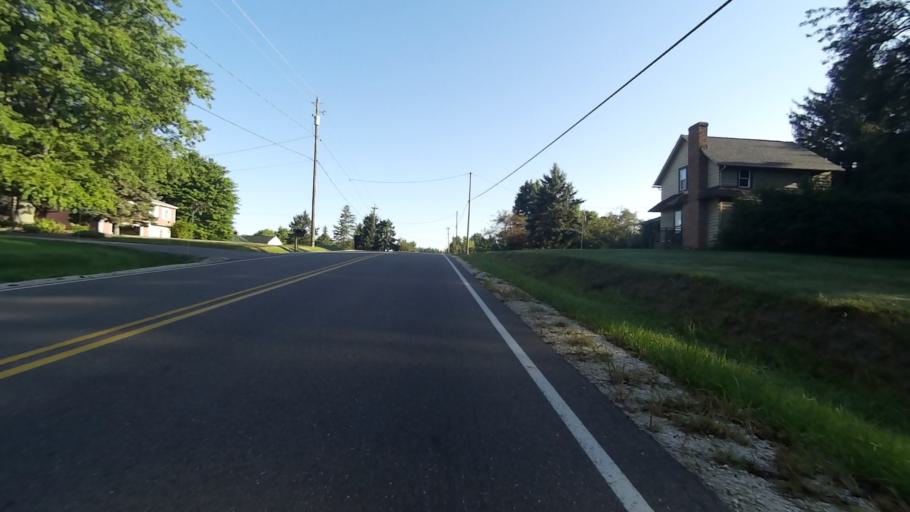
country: US
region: Ohio
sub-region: Portage County
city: Kent
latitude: 41.1867
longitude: -81.3653
